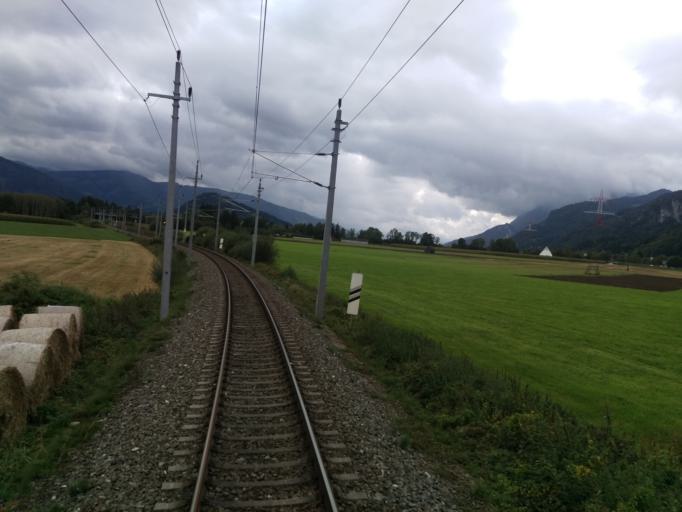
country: AT
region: Styria
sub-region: Politischer Bezirk Liezen
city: Worschach
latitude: 47.5548
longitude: 14.1612
